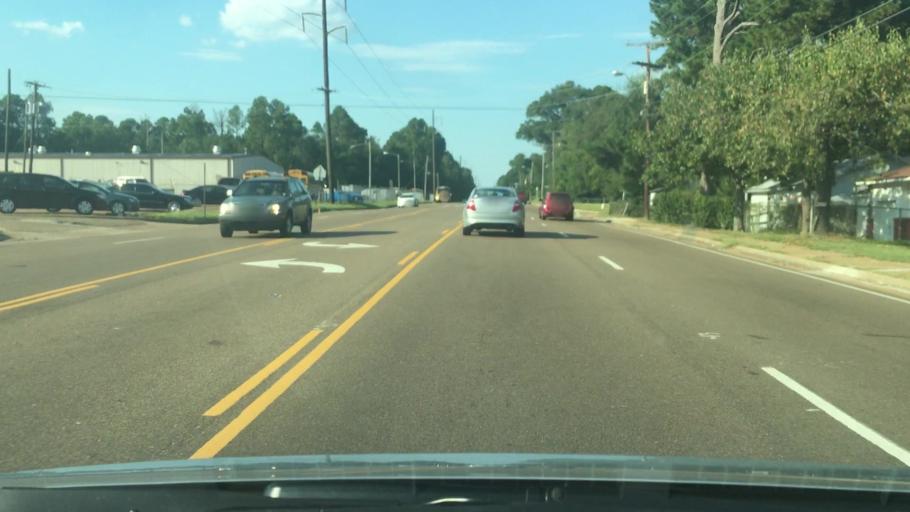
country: US
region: Mississippi
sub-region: Hinds County
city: Jackson
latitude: 32.3584
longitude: -90.1927
